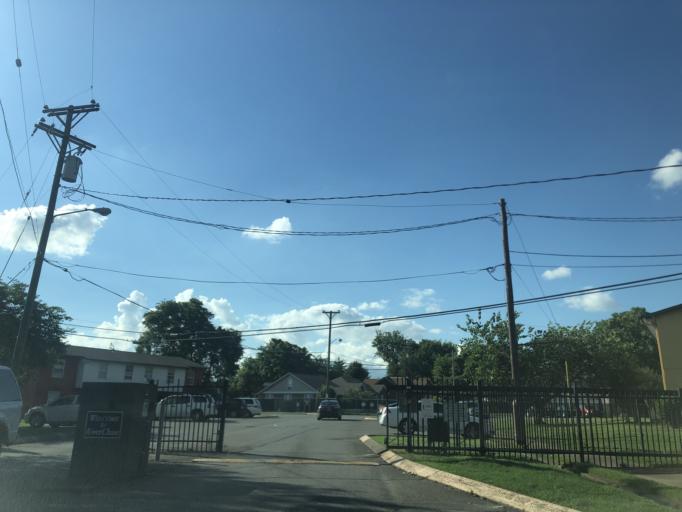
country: US
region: Tennessee
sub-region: Davidson County
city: Nashville
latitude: 36.1790
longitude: -86.7716
